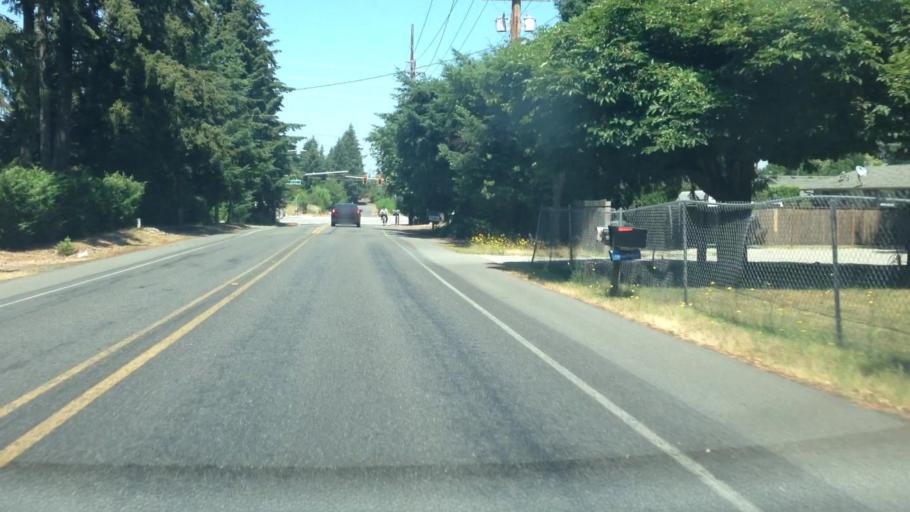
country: US
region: Washington
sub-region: Pierce County
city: Puyallup
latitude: 47.1536
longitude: -122.3148
